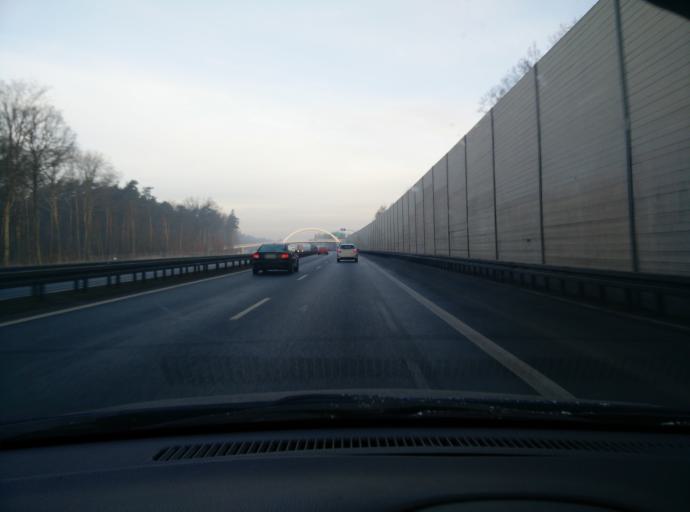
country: PL
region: Greater Poland Voivodeship
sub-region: Powiat poznanski
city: Kornik
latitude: 52.2925
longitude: 17.0544
